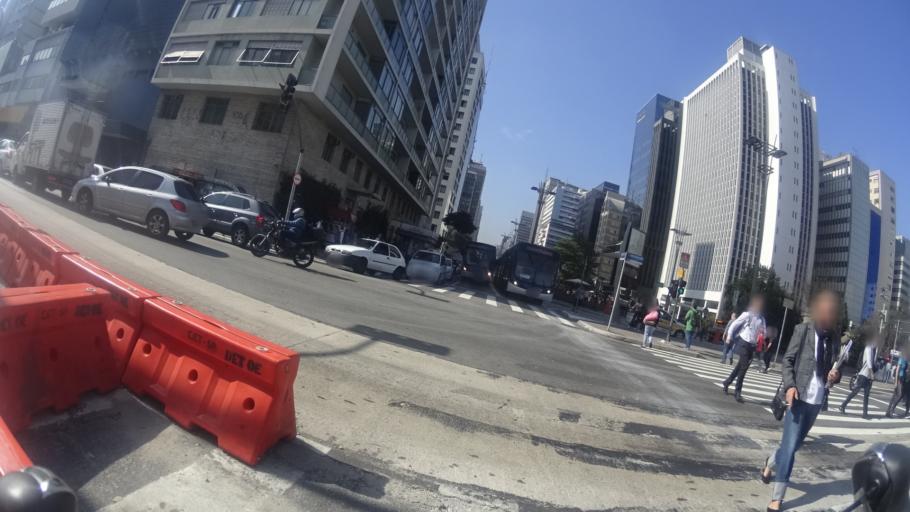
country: BR
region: Sao Paulo
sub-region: Sao Paulo
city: Sao Paulo
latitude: -23.5555
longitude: -46.6686
